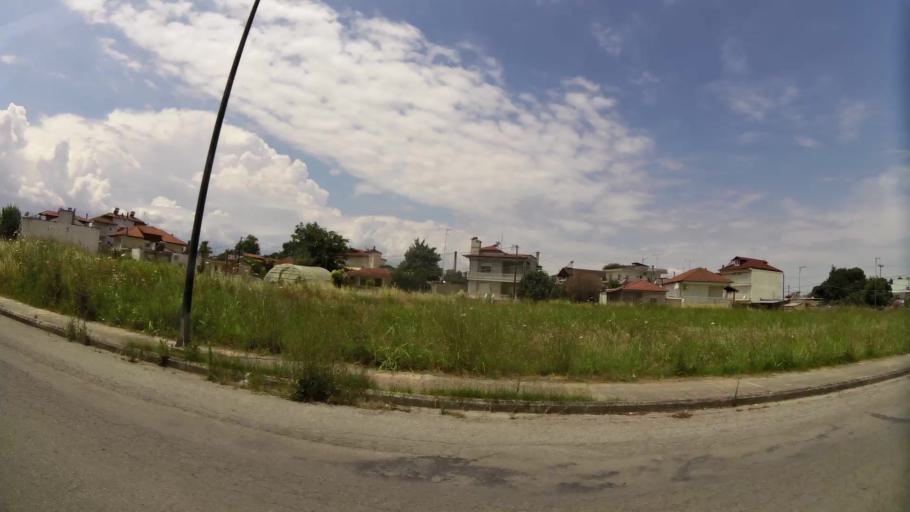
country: GR
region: Central Macedonia
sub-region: Nomos Pierias
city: Peristasi
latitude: 40.2674
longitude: 22.5348
